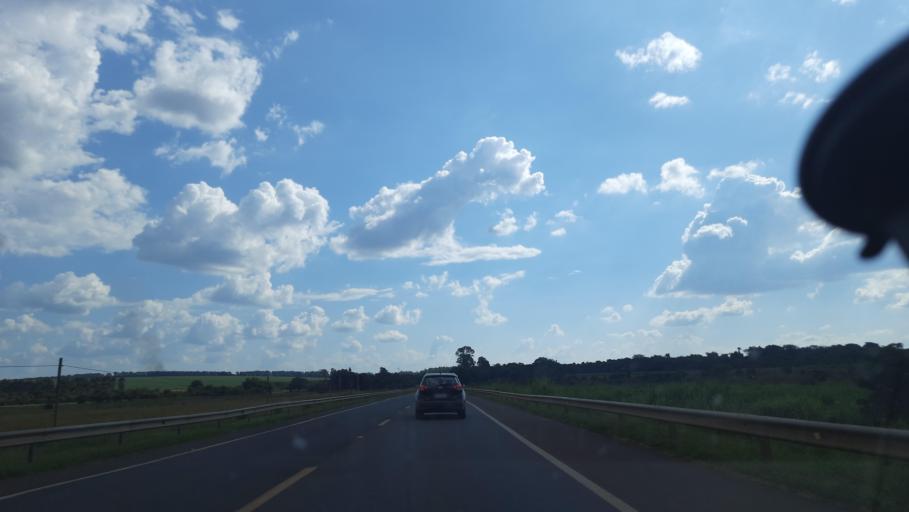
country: BR
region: Sao Paulo
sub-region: Casa Branca
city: Casa Branca
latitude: -21.7471
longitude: -46.9883
